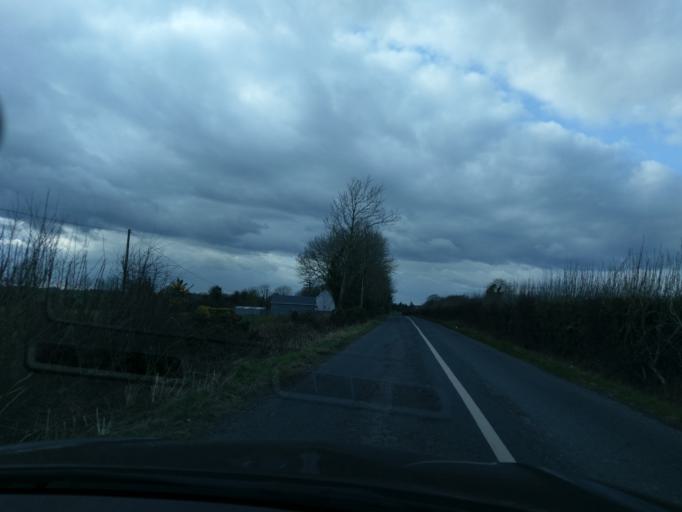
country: IE
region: Connaught
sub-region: County Galway
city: Athenry
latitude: 53.4890
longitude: -8.5888
